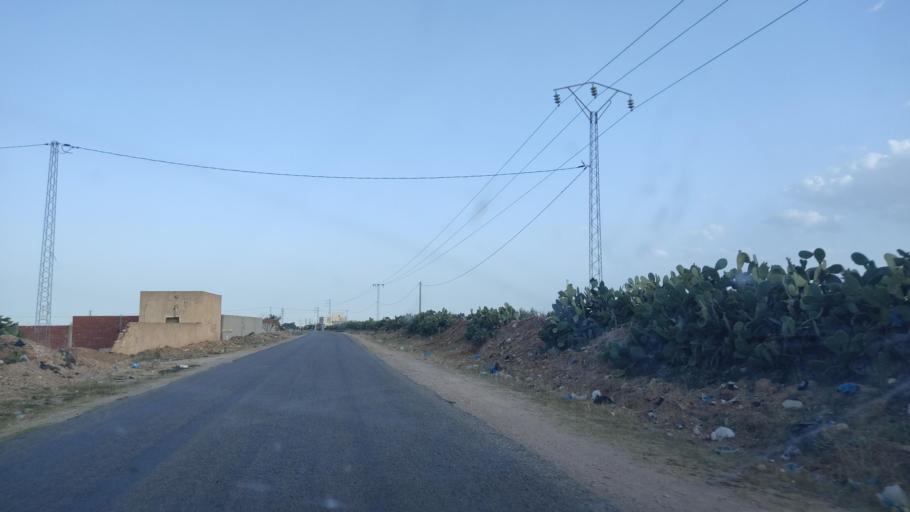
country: TN
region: Safaqis
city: Sfax
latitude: 34.8141
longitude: 10.6579
